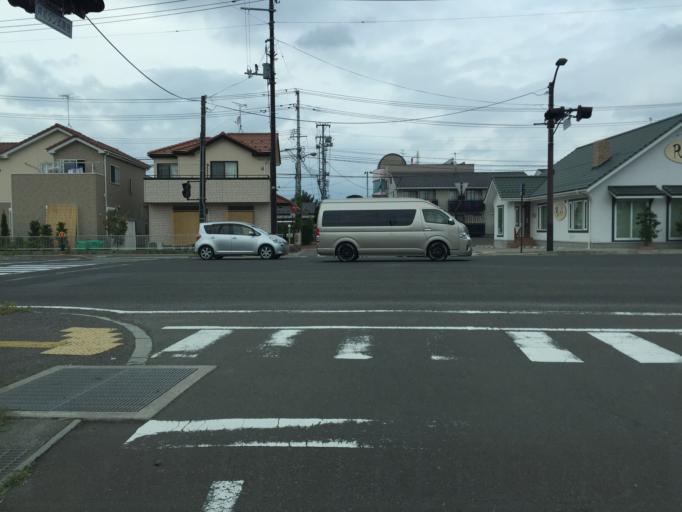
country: JP
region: Fukushima
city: Fukushima-shi
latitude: 37.7289
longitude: 140.4480
